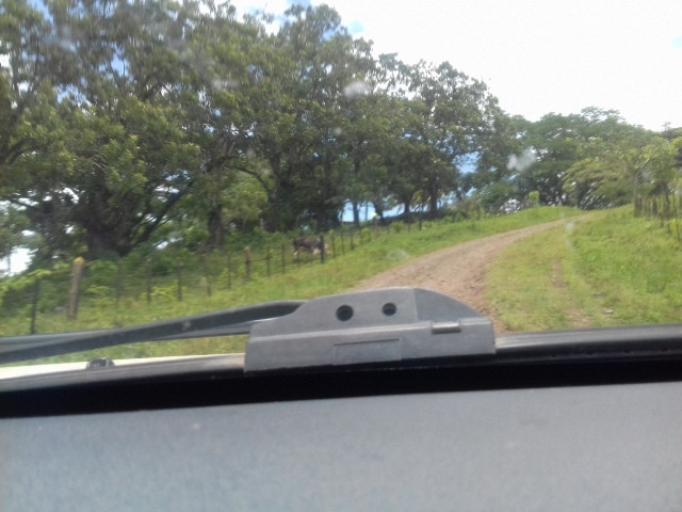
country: NI
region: Matagalpa
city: Matiguas
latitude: 13.0211
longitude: -85.4058
